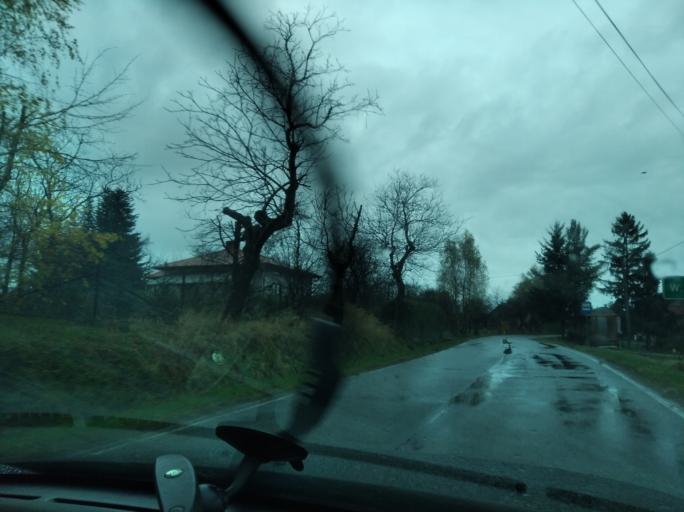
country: PL
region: Subcarpathian Voivodeship
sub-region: Powiat lancucki
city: Handzlowka
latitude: 49.9879
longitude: 22.1895
